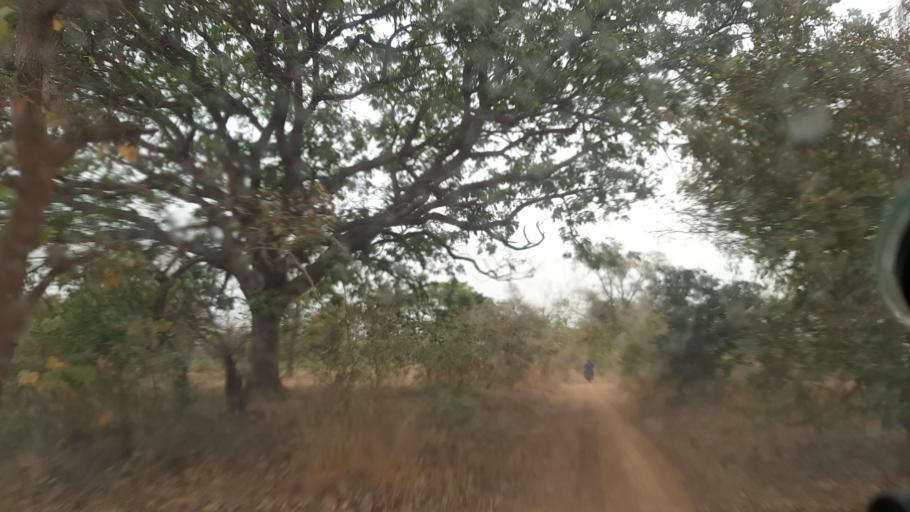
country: BF
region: Boucle du Mouhoun
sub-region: Province des Banwa
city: Salanso
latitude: 11.8542
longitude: -4.4294
